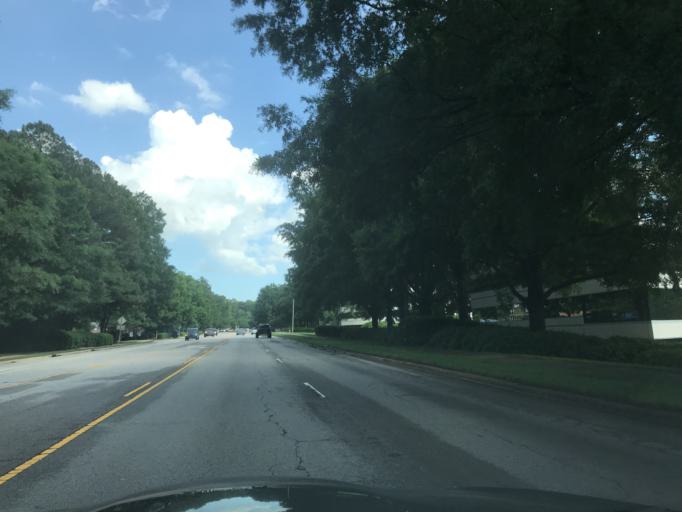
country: US
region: North Carolina
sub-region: Wake County
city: West Raleigh
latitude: 35.8711
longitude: -78.6413
